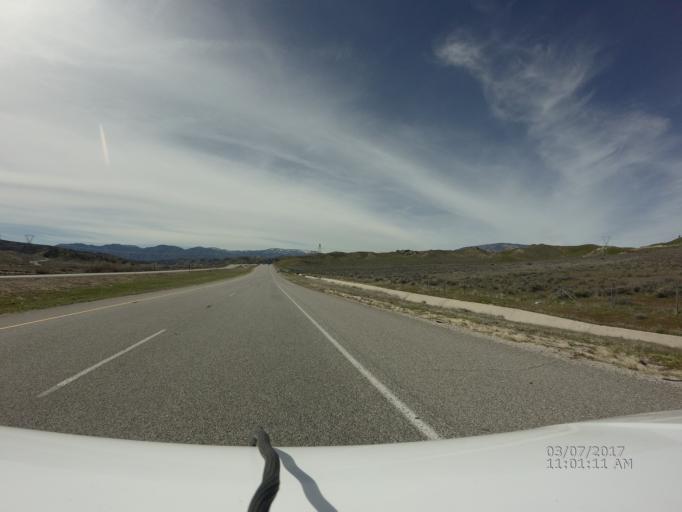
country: US
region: California
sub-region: Kern County
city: Lebec
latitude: 34.7727
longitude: -118.7790
